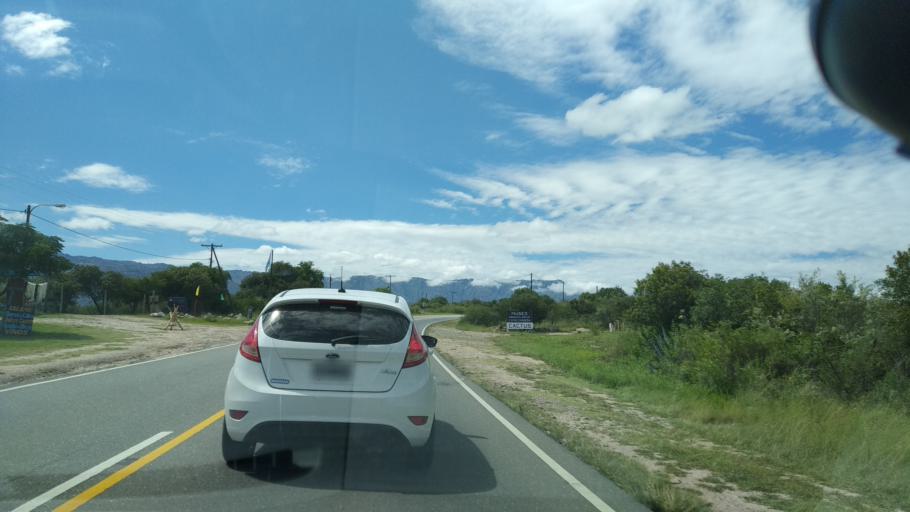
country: AR
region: Cordoba
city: Mina Clavero
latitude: -31.7587
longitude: -64.9727
